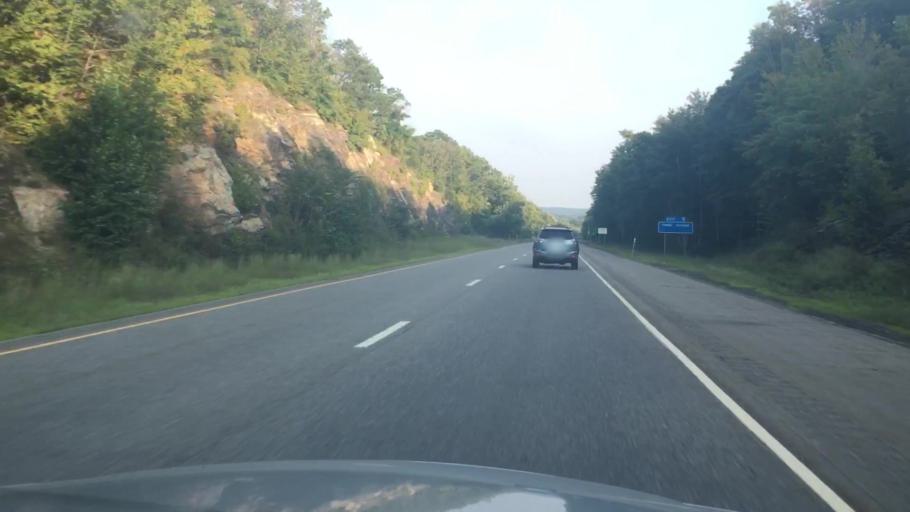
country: US
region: Connecticut
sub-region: Middlesex County
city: Chester Center
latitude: 41.3910
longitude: -72.4605
